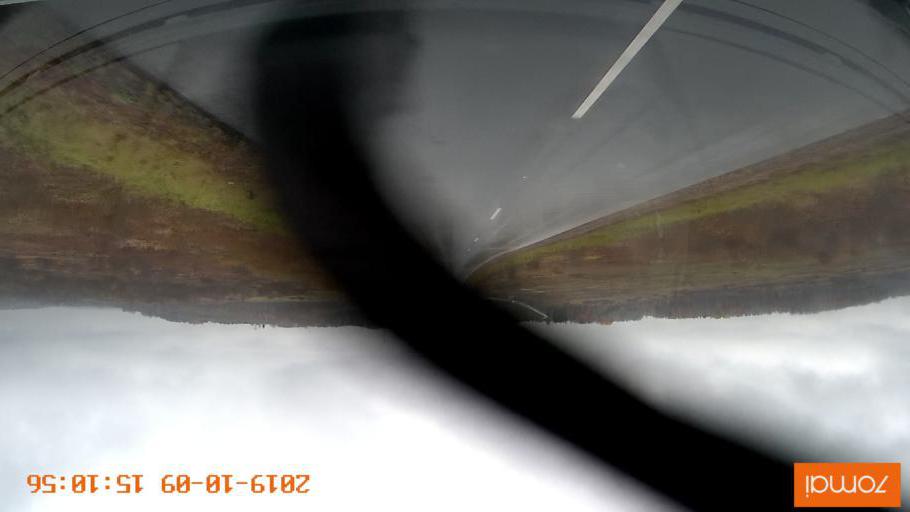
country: RU
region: Kostroma
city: Susanino
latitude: 58.1719
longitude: 41.6342
